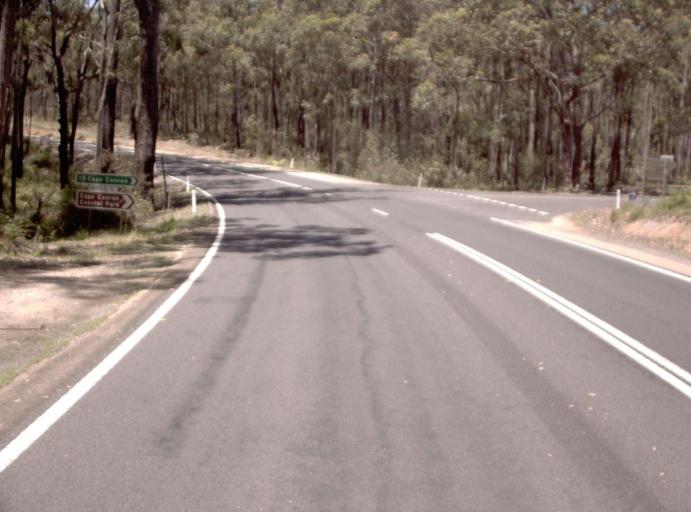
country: AU
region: Victoria
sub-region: East Gippsland
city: Lakes Entrance
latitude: -37.6956
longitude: 148.7419
